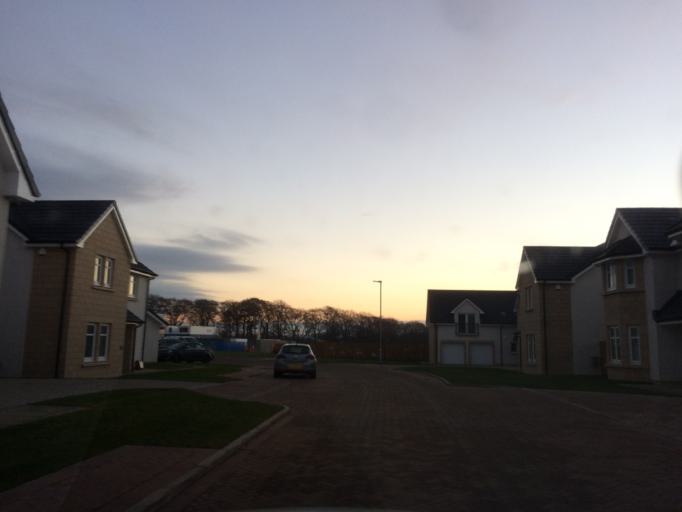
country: GB
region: Scotland
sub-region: East Renfrewshire
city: Newton Mearns
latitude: 55.7914
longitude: -4.3278
